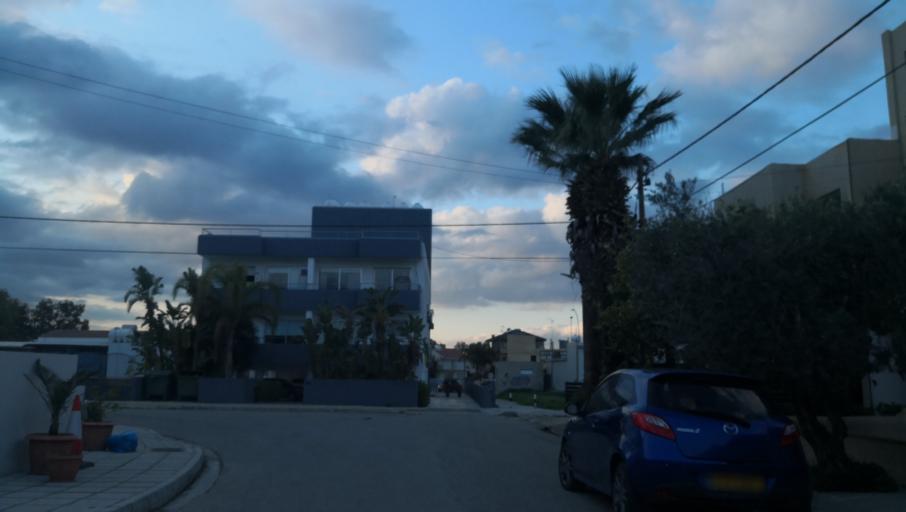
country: CY
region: Lefkosia
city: Kato Deftera
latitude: 35.0993
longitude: 33.2993
